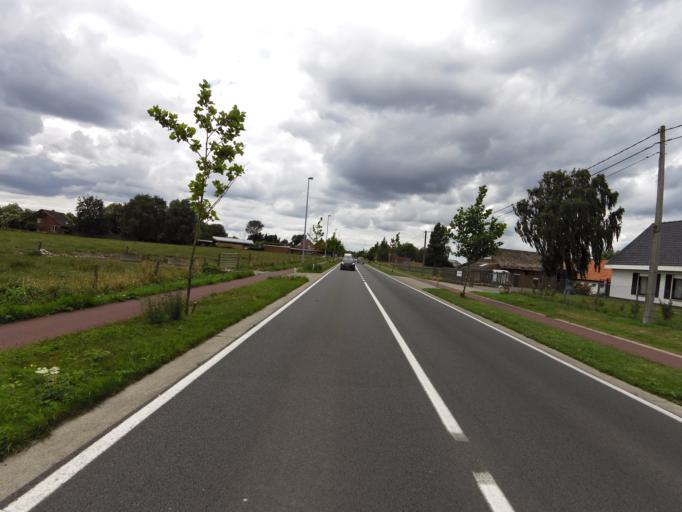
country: BE
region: Flanders
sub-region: Provincie West-Vlaanderen
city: Hooglede
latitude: 50.9590
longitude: 3.0737
